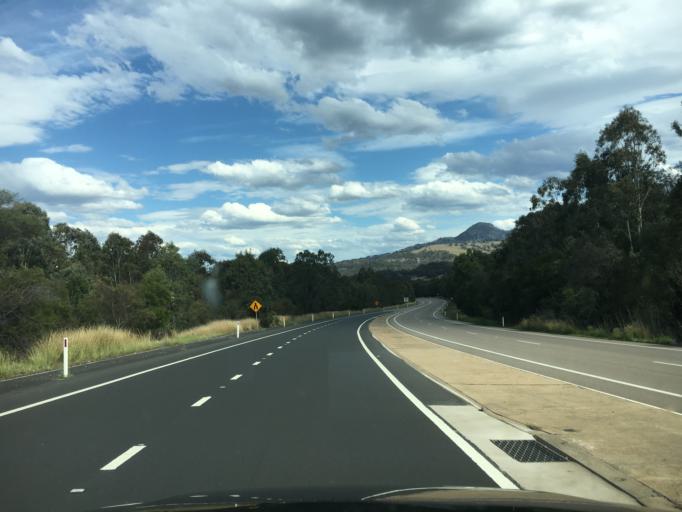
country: AU
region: New South Wales
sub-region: Liverpool Plains
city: Quirindi
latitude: -31.7510
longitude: 150.8128
